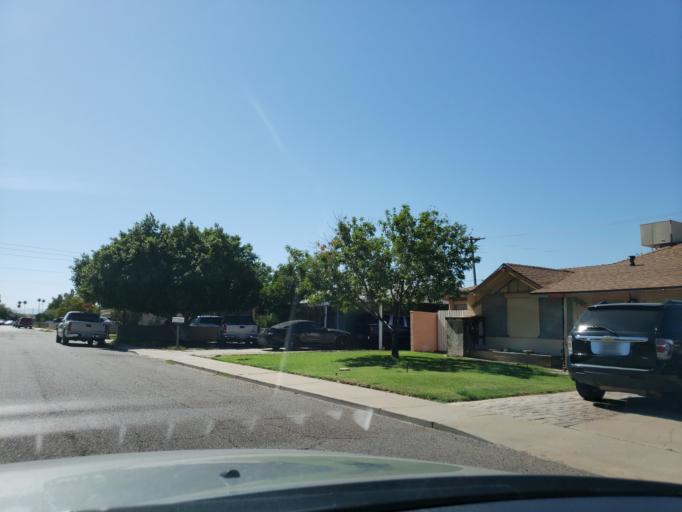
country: US
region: Arizona
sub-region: Maricopa County
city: Glendale
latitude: 33.4738
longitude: -112.1643
